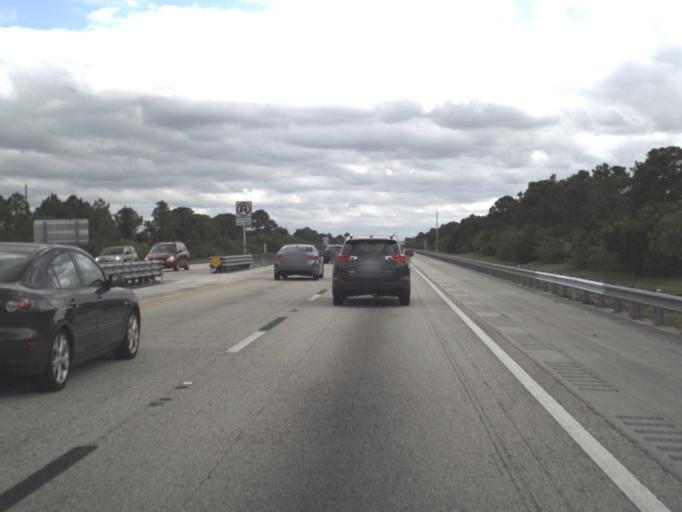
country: US
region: Florida
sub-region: Martin County
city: Palm City
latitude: 27.1369
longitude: -80.2881
